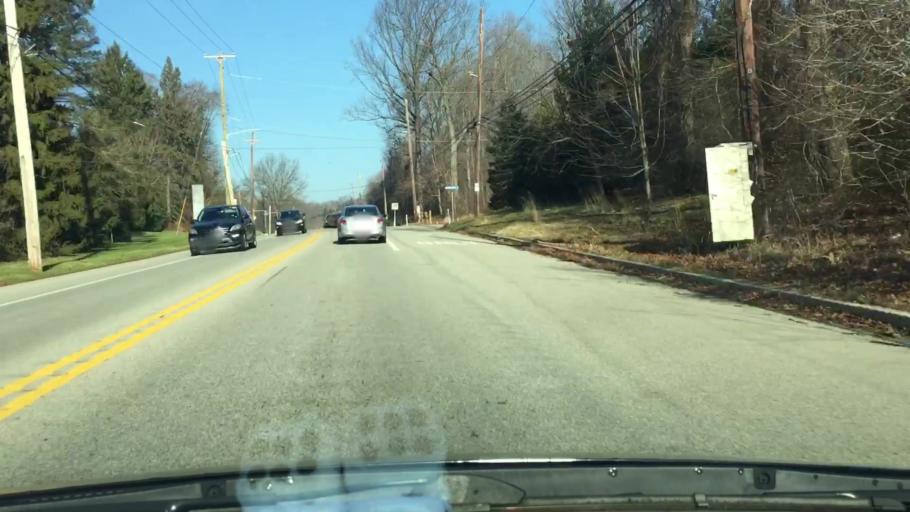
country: US
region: Pennsylvania
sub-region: Delaware County
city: Broomall
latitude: 39.9599
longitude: -75.3941
